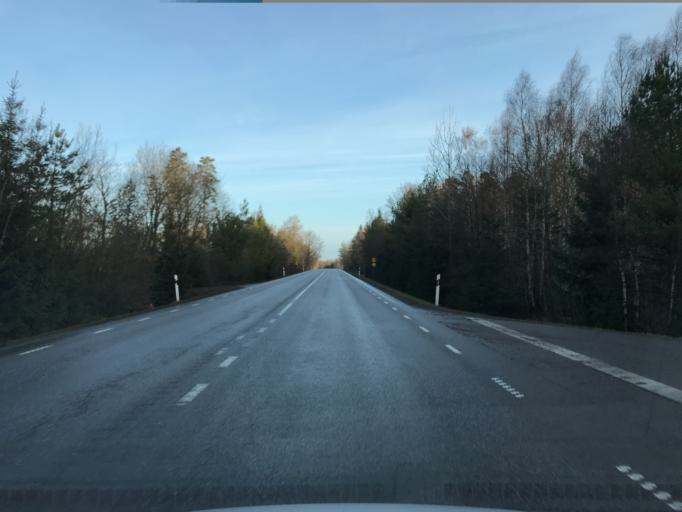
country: SE
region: Skane
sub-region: Hassleholms Kommun
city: Bjarnum
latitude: 56.2481
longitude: 13.7157
